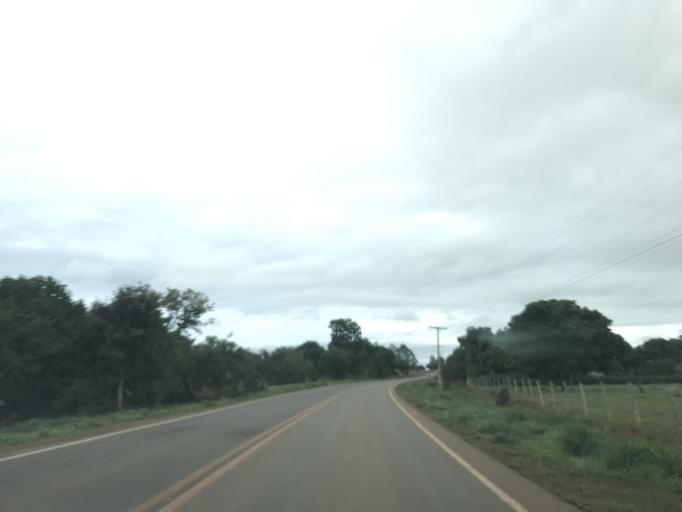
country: BR
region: Goias
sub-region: Luziania
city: Luziania
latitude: -16.3249
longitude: -48.0195
